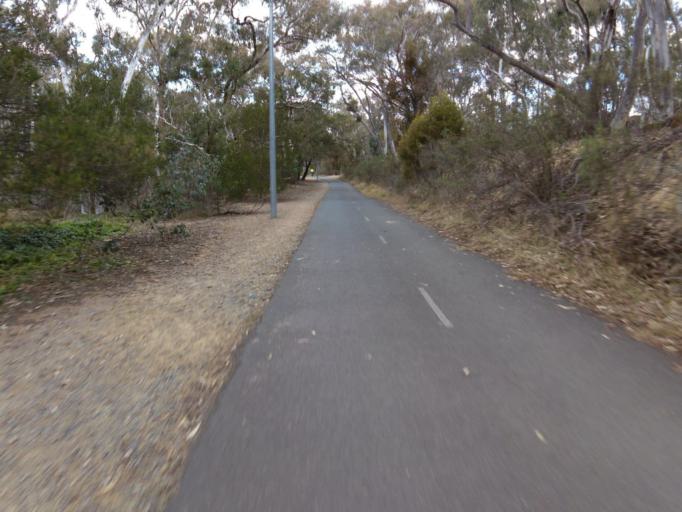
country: AU
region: Australian Capital Territory
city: Acton
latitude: -35.2539
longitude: 149.1087
